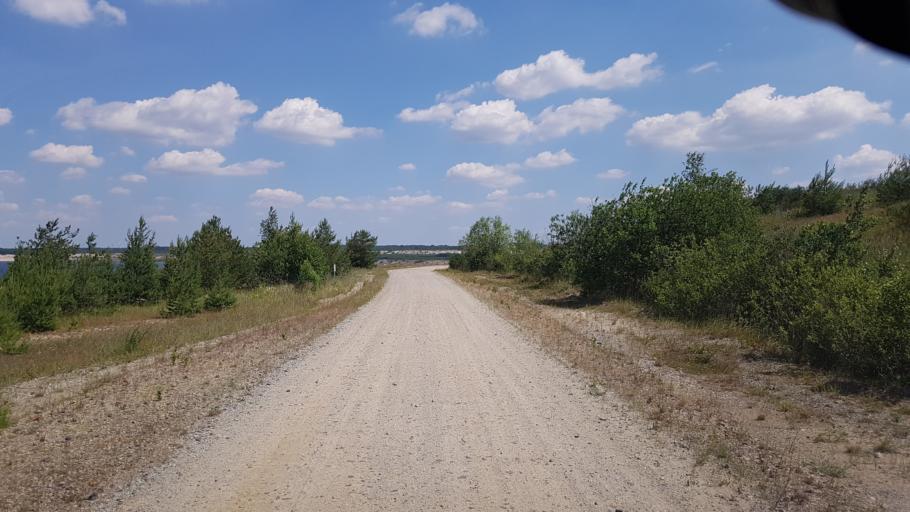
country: DE
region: Brandenburg
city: Sallgast
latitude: 51.5568
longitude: 13.7873
